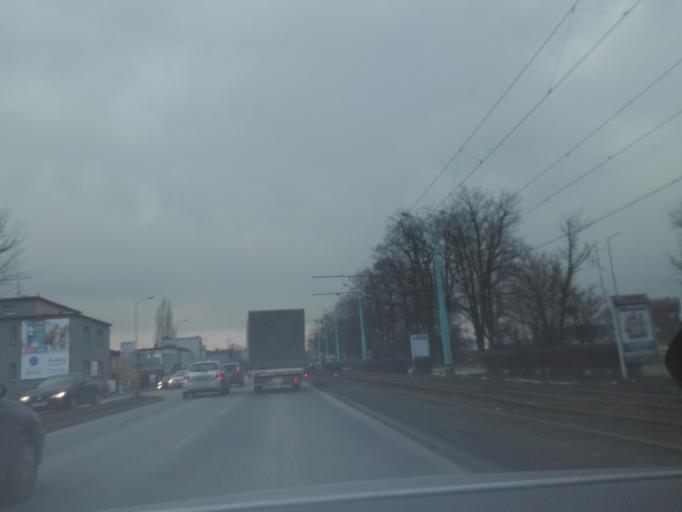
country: PL
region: Silesian Voivodeship
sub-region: Chorzow
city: Chorzow
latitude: 50.2883
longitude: 18.9665
